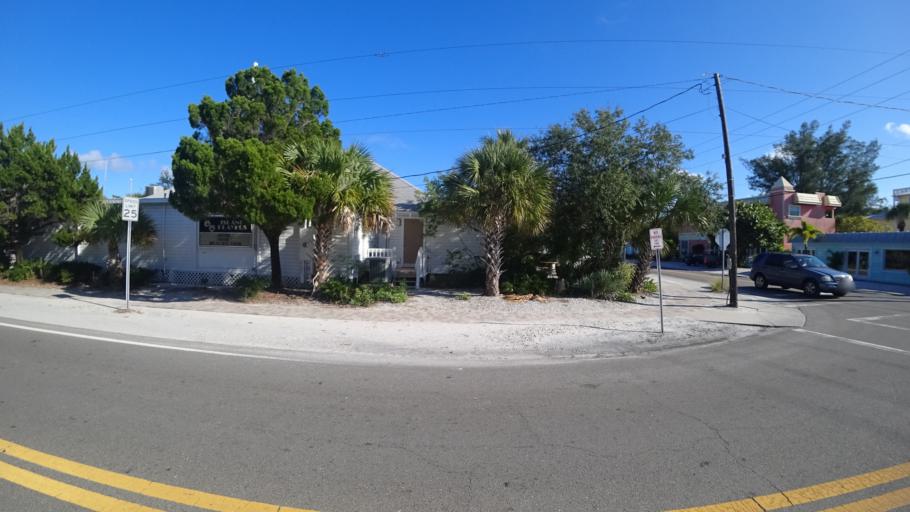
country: US
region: Florida
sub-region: Manatee County
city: Anna Maria
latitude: 27.5270
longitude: -82.7367
